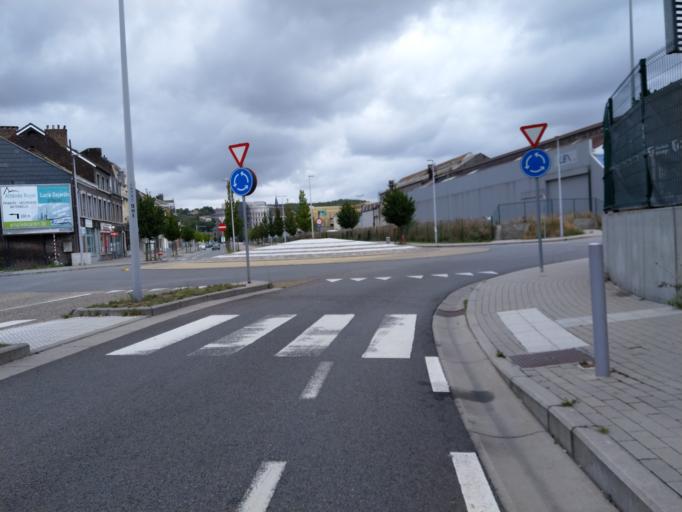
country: BE
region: Wallonia
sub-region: Province de Liege
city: Saint-Nicolas
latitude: 50.6119
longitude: 5.5125
